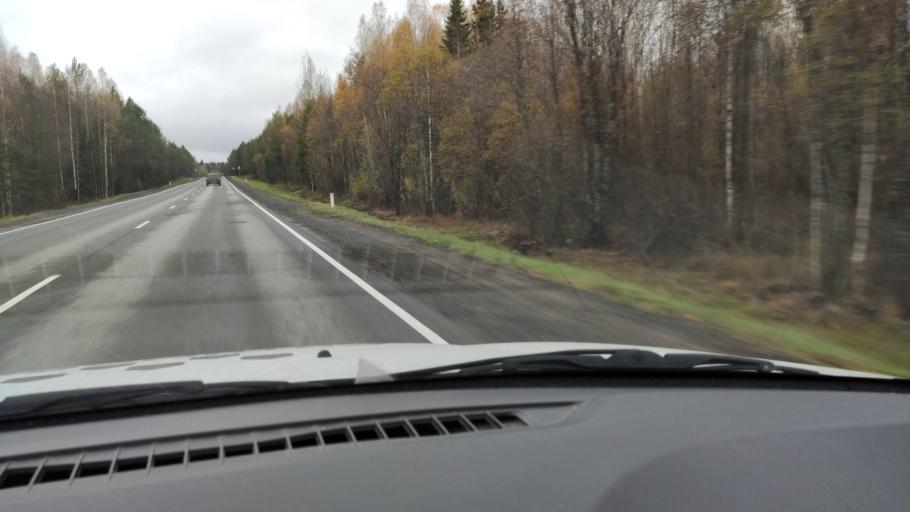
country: RU
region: Kirov
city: Belaya Kholunitsa
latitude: 58.8992
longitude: 50.9268
